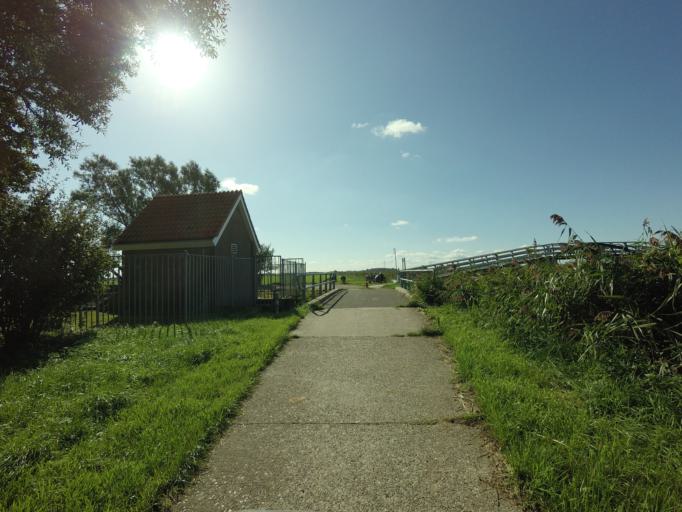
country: NL
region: Friesland
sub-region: Gemeente Boarnsterhim
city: Reduzum
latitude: 53.1206
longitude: 5.7564
